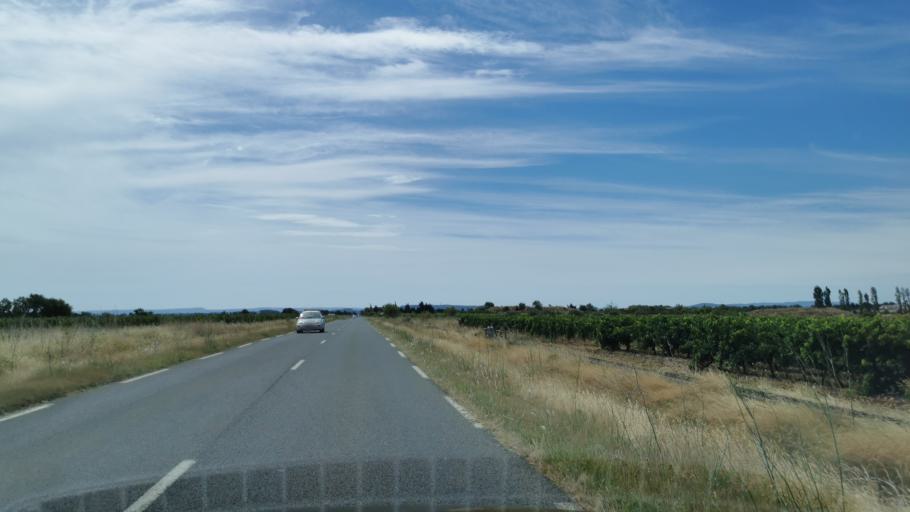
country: FR
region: Languedoc-Roussillon
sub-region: Departement de l'Aude
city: Ginestas
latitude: 43.2823
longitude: 2.8768
